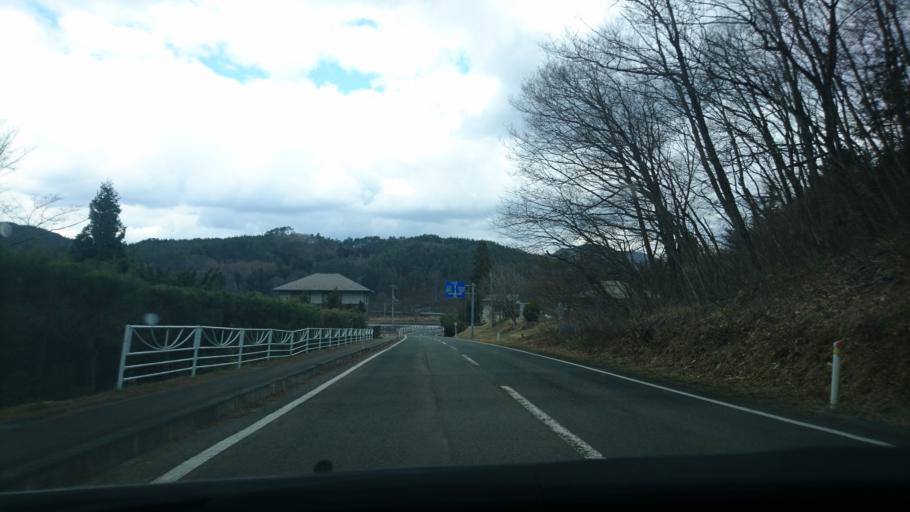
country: JP
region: Iwate
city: Tono
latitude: 39.3513
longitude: 141.3434
